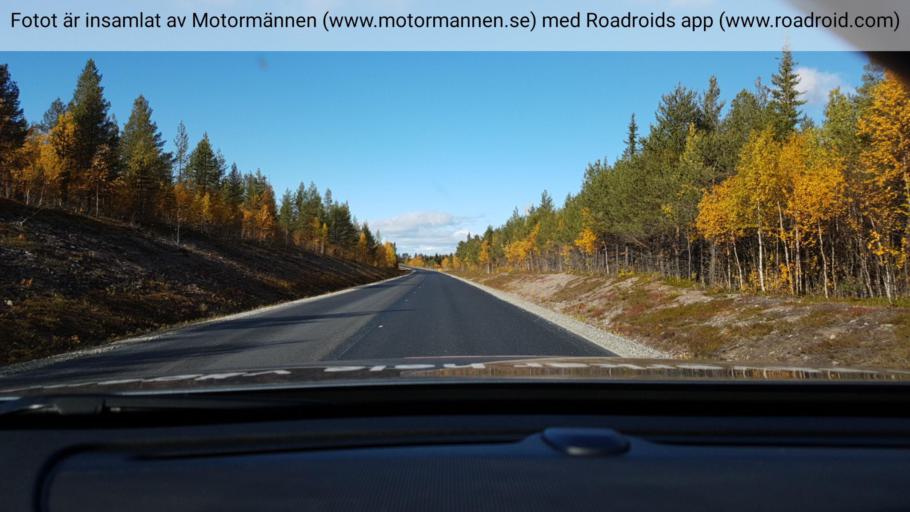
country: SE
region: Norrbotten
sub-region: Arjeplogs Kommun
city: Arjeplog
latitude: 65.9737
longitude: 18.2441
